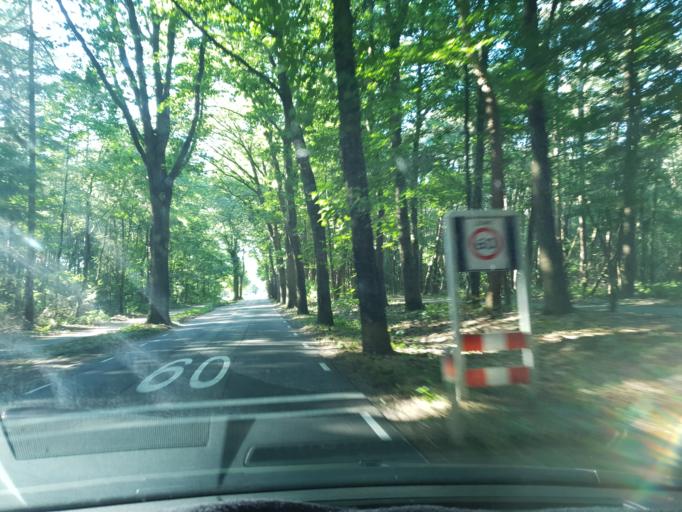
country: NL
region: North Brabant
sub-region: Gemeente Rucphen
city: Rucphen
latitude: 51.5140
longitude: 4.5772
